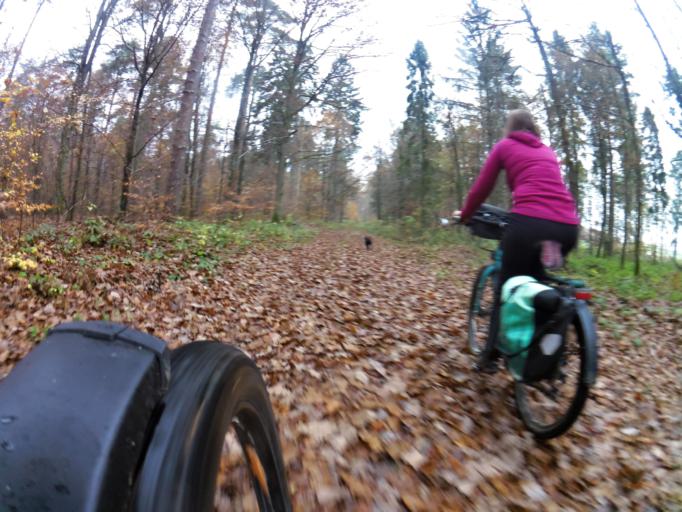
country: PL
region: Pomeranian Voivodeship
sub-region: Powiat pucki
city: Krokowa
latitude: 54.7361
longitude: 18.1303
